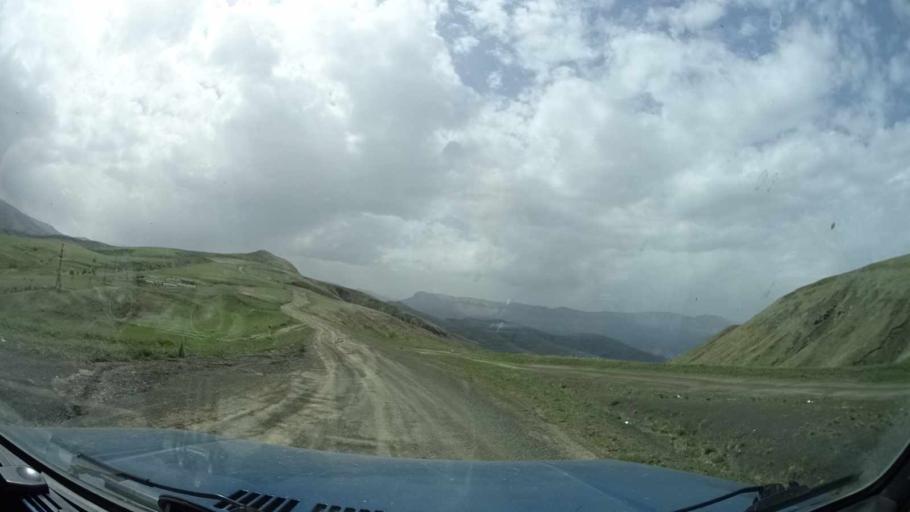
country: RU
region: Dagestan
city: Kubachi
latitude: 42.0811
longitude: 47.5554
